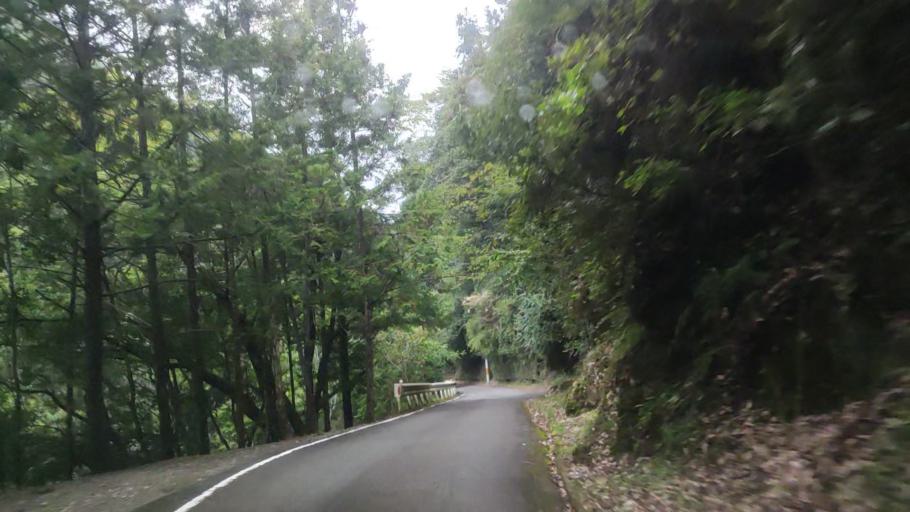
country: JP
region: Wakayama
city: Koya
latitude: 34.2617
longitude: 135.6492
